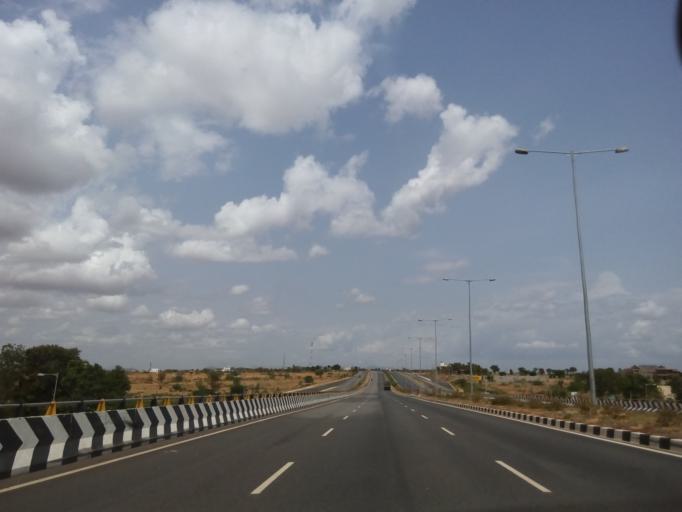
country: IN
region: Karnataka
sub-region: Tumkur
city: Sira
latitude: 13.7590
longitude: 76.8735
